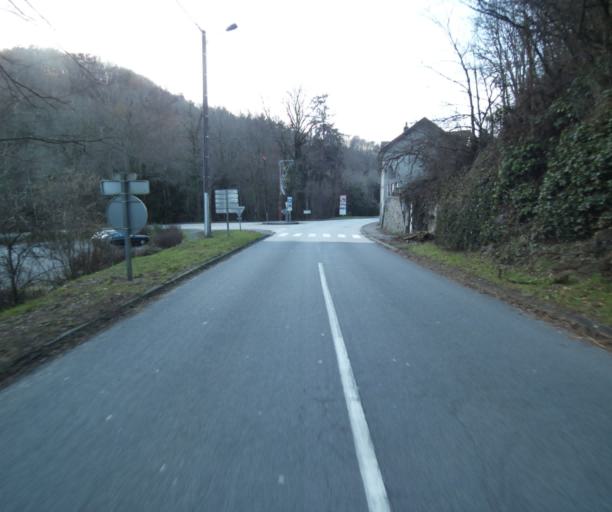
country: FR
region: Limousin
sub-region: Departement de la Correze
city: Laguenne
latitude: 45.2406
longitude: 1.7857
